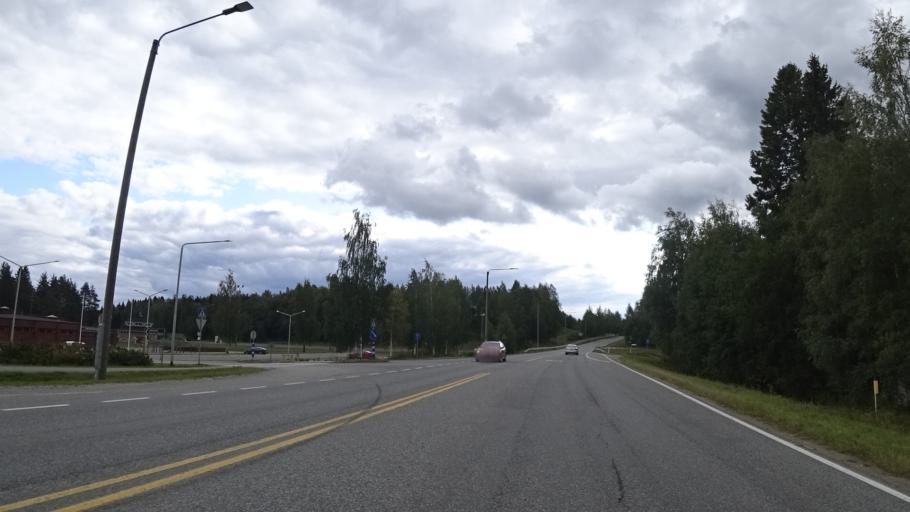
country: FI
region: North Karelia
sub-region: Joensuu
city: Ilomantsi
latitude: 62.6625
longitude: 30.9355
